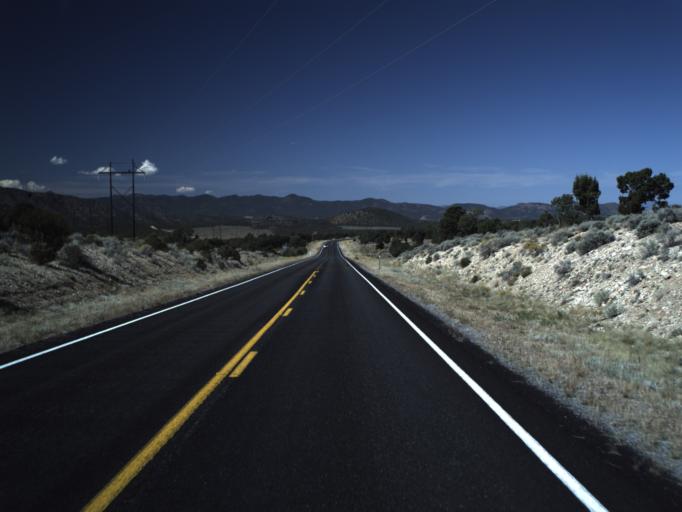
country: US
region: Utah
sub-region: Washington County
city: Enterprise
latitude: 37.6112
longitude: -113.3908
